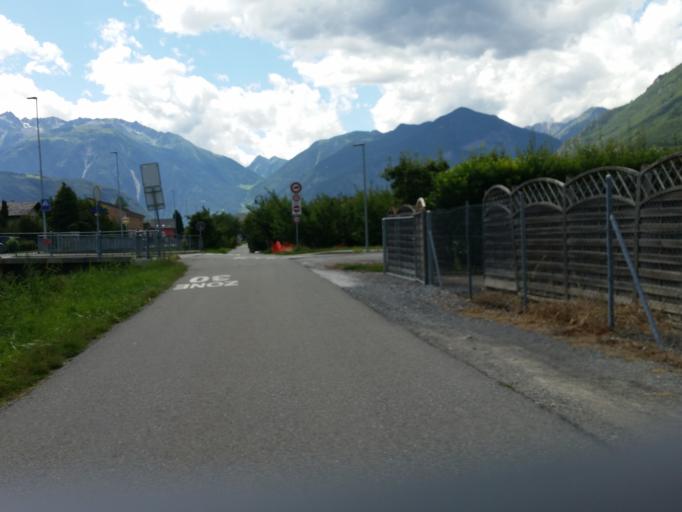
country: CH
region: Valais
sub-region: Martigny District
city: Fully
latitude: 46.1404
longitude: 7.1203
